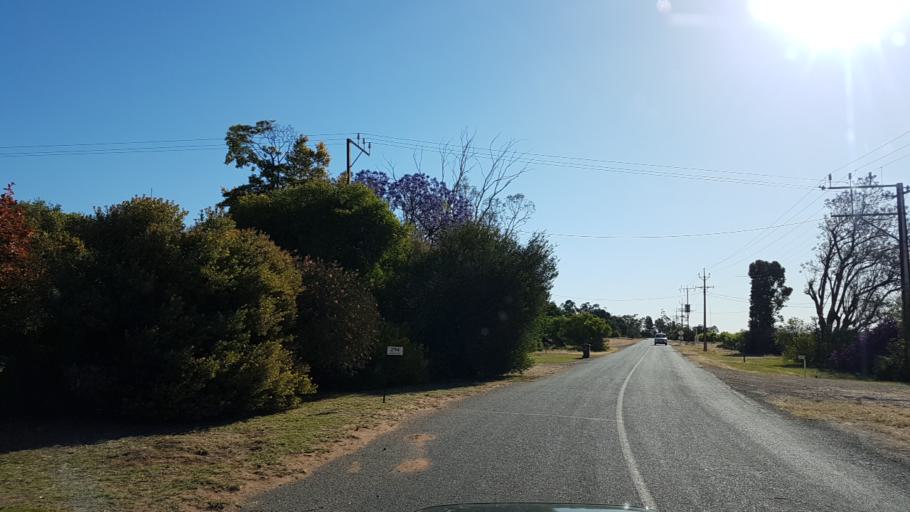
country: AU
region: South Australia
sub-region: Loxton Waikerie
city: Waikerie
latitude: -34.1689
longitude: 140.0368
